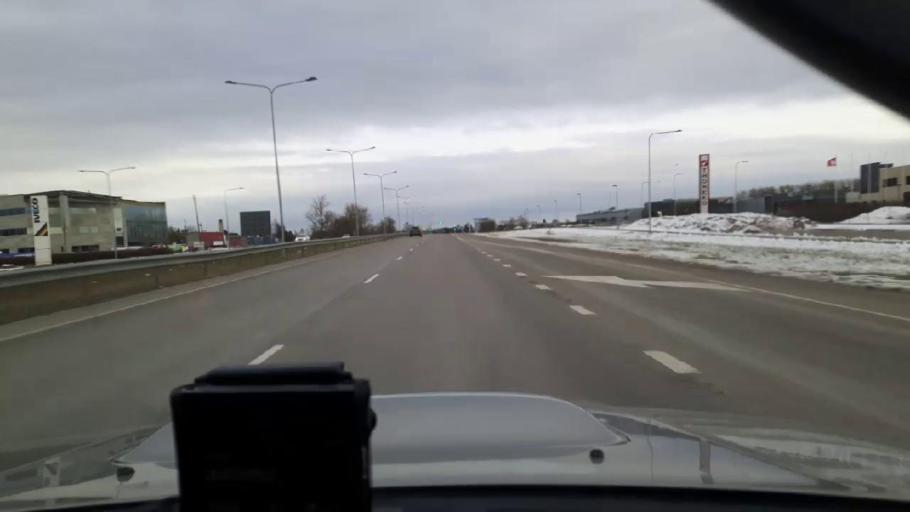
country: EE
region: Harju
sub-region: Saue vald
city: Laagri
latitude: 59.3428
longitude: 24.6180
